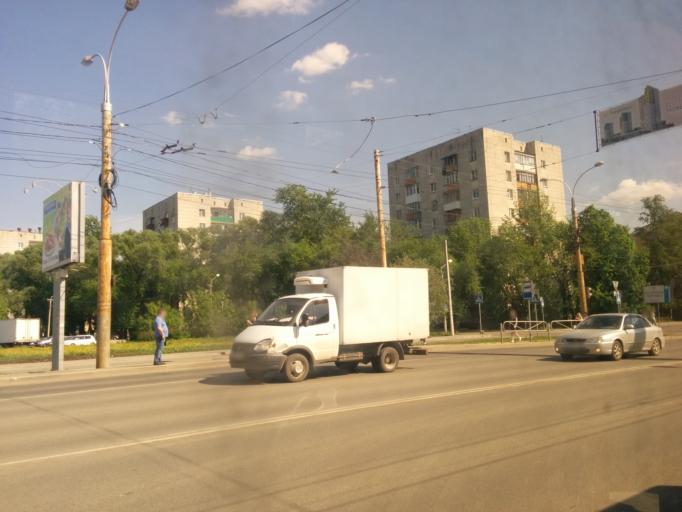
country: RU
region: Perm
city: Perm
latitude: 58.0040
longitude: 56.2864
